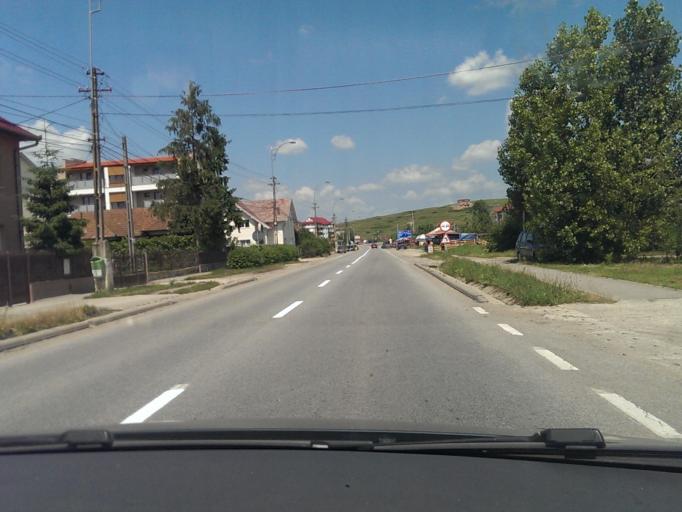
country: RO
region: Cluj
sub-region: Comuna Apahida
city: Apahida
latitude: 46.7977
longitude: 23.7521
